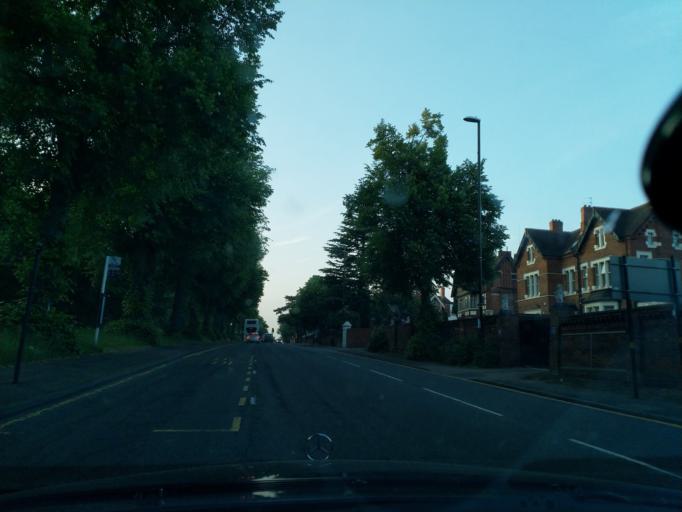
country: GB
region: England
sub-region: Coventry
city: Coventry
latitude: 52.3972
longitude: -1.5168
